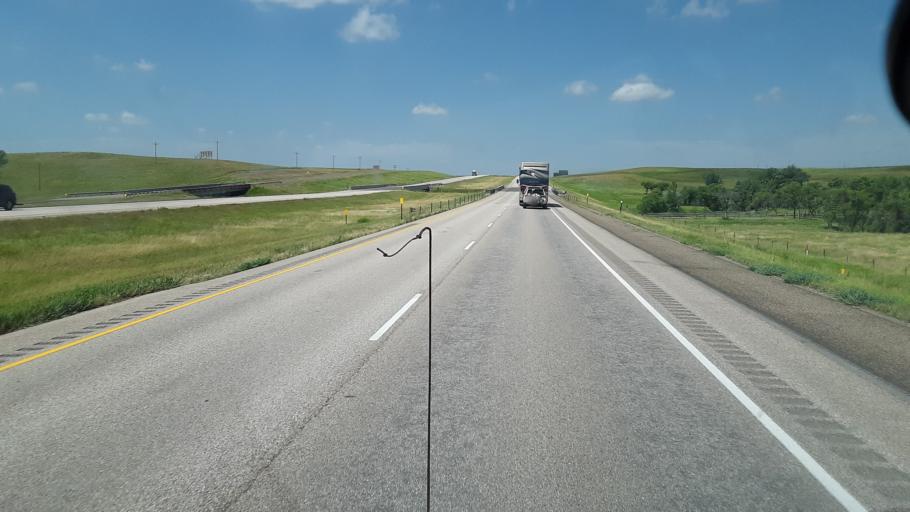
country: US
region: South Dakota
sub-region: Jackson County
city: Kadoka
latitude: 43.8364
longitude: -101.5497
